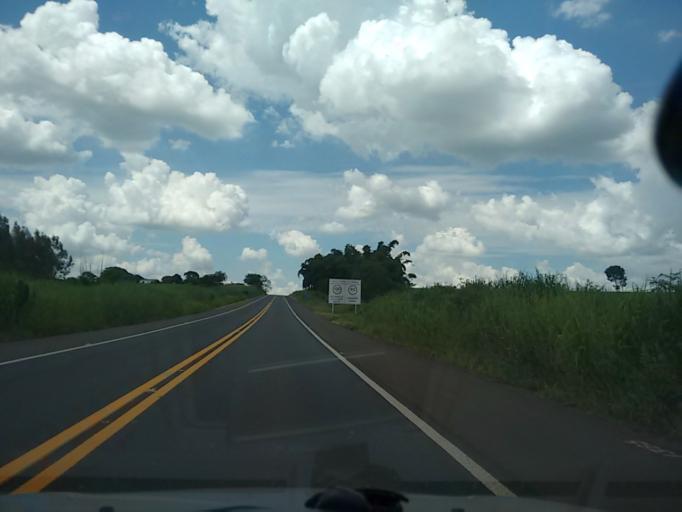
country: BR
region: Sao Paulo
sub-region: Osvaldo Cruz
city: Osvaldo Cruz
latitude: -21.8472
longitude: -50.8338
